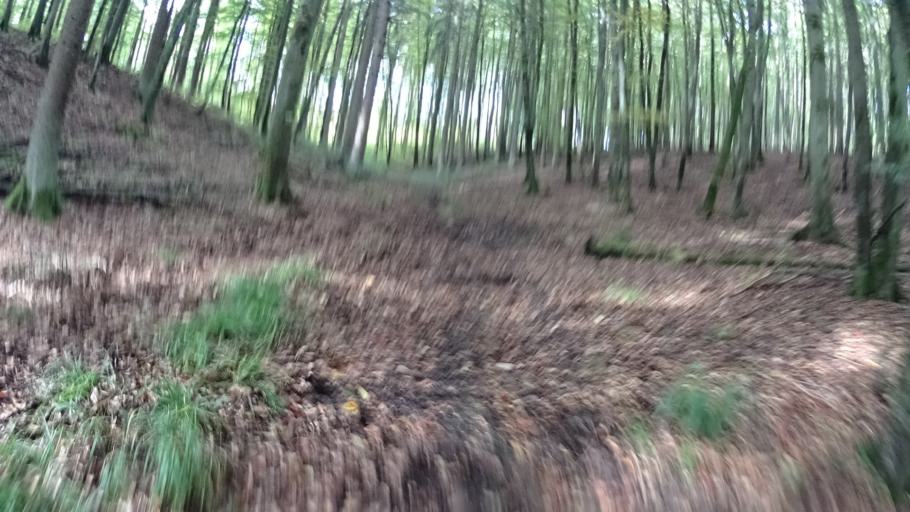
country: DE
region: Bavaria
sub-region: Upper Bavaria
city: Bohmfeld
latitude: 48.8923
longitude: 11.3363
